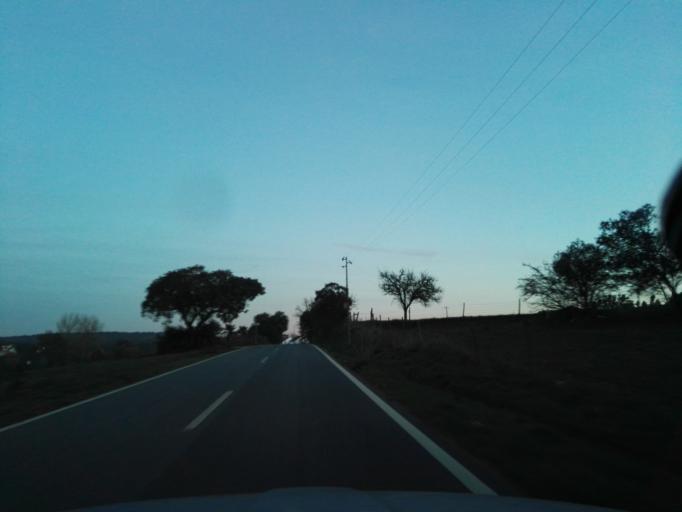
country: PT
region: Evora
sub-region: Arraiolos
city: Arraiolos
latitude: 38.7409
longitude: -8.0801
